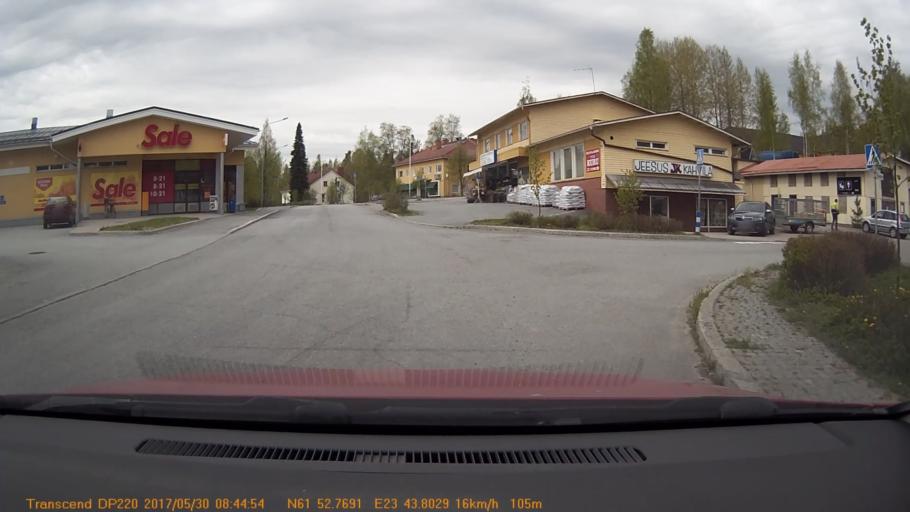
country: FI
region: Pirkanmaa
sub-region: Tampere
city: Kuru
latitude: 61.8795
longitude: 23.7301
